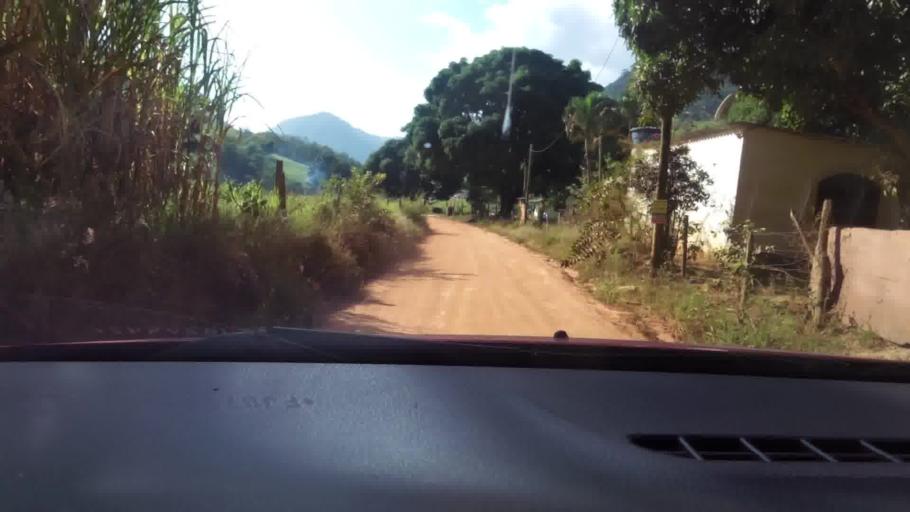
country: BR
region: Espirito Santo
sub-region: Guarapari
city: Guarapari
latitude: -20.5381
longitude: -40.5606
